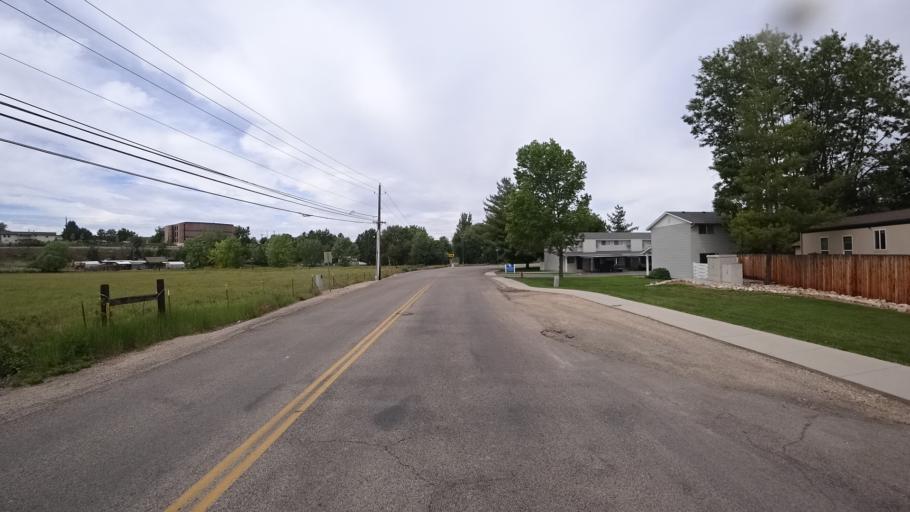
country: US
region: Idaho
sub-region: Ada County
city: Boise
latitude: 43.5754
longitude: -116.2108
